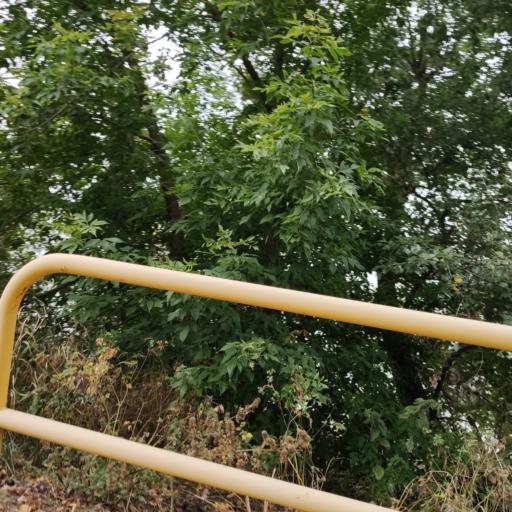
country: PL
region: Kujawsko-Pomorskie
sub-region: Powiat zninski
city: Znin
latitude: 52.8567
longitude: 17.7526
